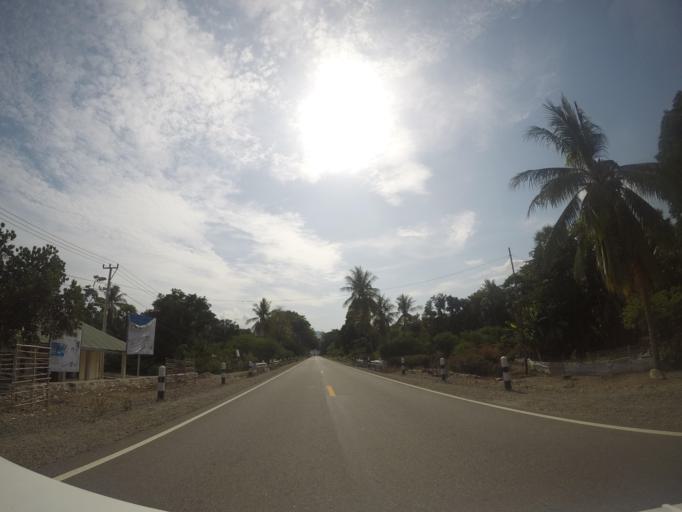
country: ID
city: Metinaro
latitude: -8.5306
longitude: 125.7418
